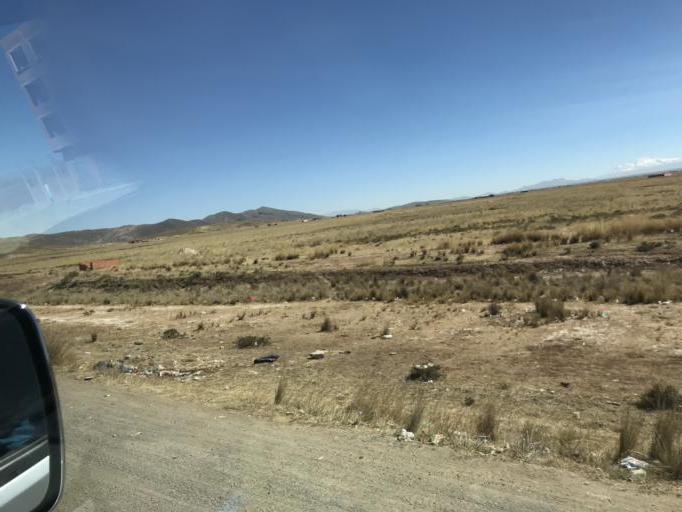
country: BO
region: La Paz
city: La Paz
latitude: -16.5312
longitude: -68.3890
